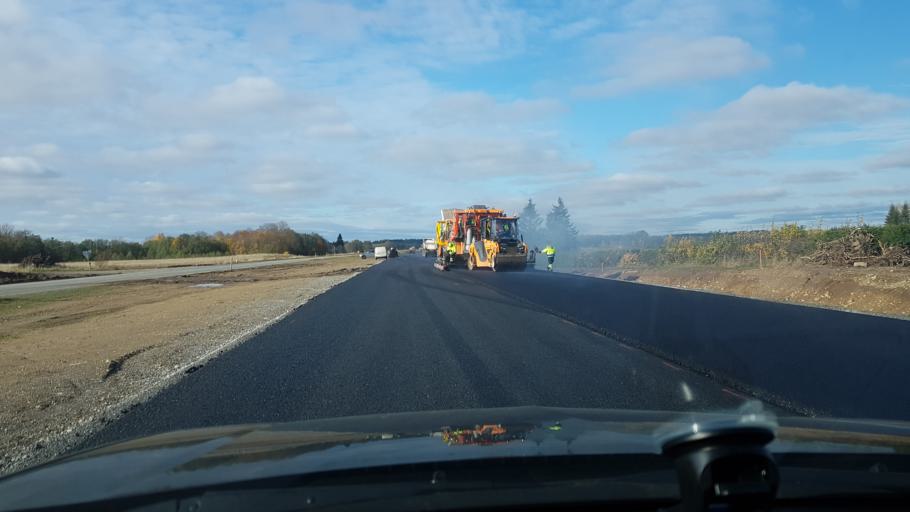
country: EE
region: Laeaene-Virumaa
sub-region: Kadrina vald
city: Kadrina
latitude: 59.4405
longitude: 26.1211
